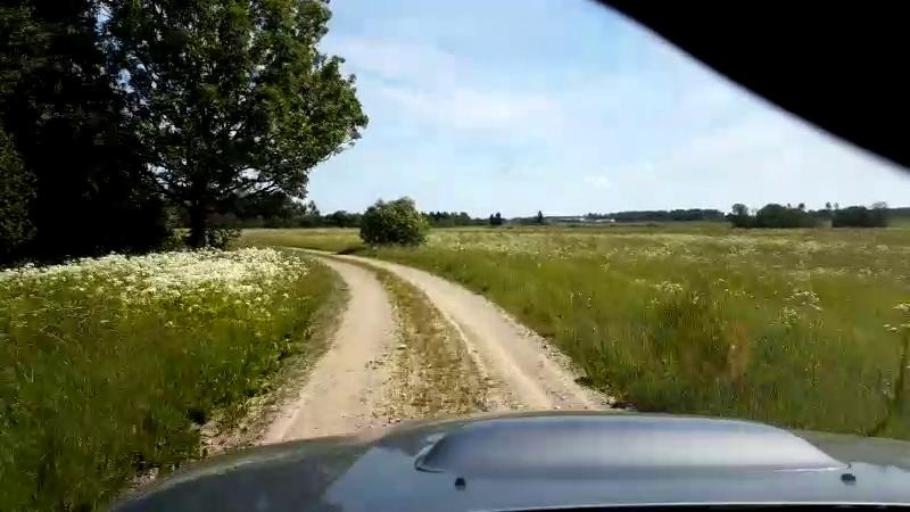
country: EE
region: Paernumaa
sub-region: Sauga vald
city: Sauga
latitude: 58.4987
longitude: 24.5429
